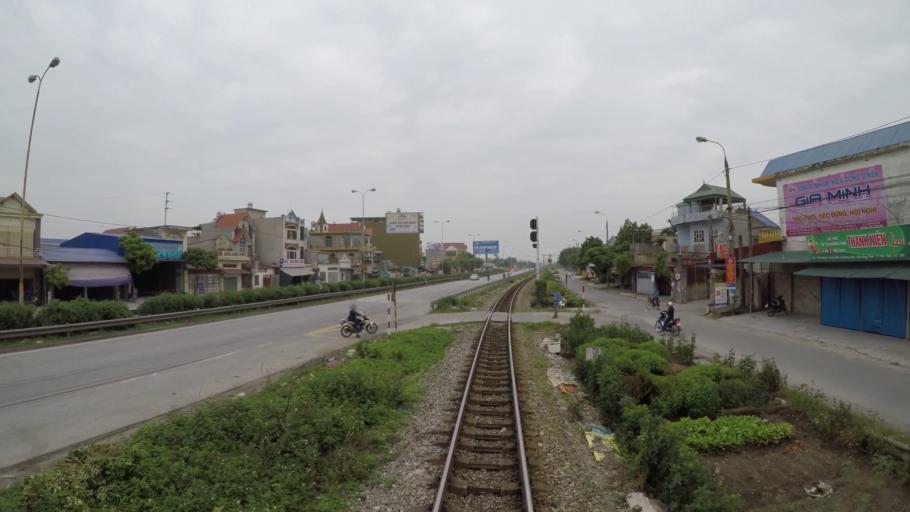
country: VN
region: Hai Duong
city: Phu Thai
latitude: 20.9670
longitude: 106.5065
